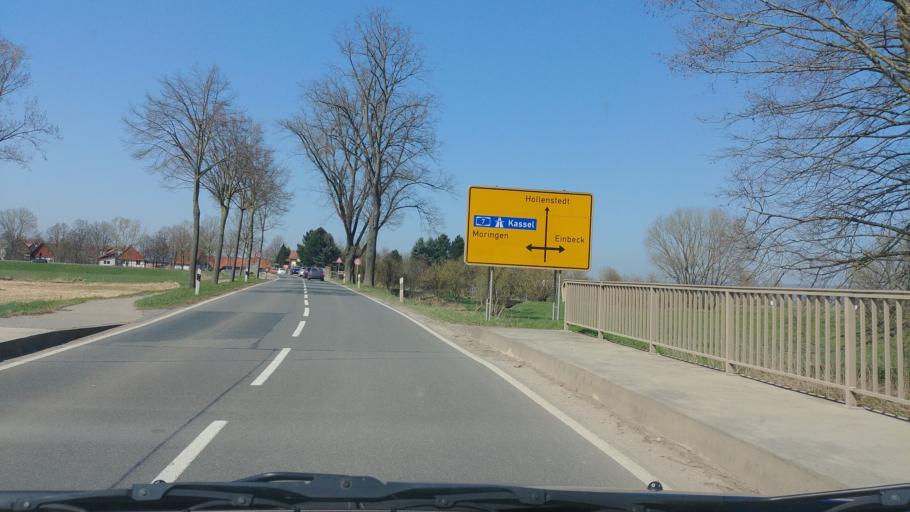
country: DE
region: Lower Saxony
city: Hillerse
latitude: 51.7374
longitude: 9.9519
